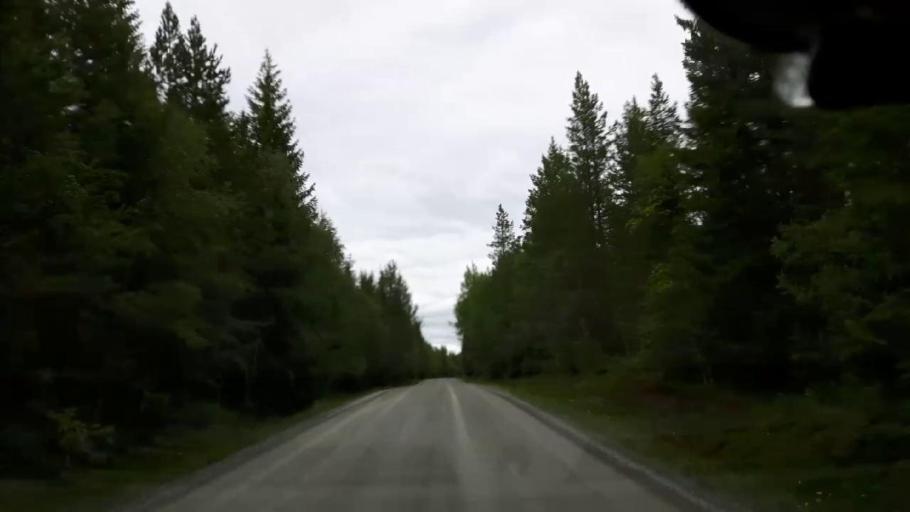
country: SE
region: Jaemtland
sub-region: OEstersunds Kommun
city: Brunflo
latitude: 63.0933
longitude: 15.1670
